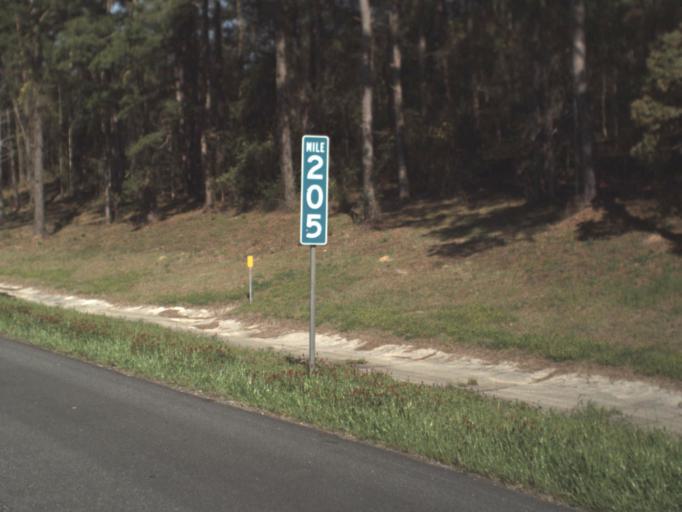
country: US
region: Florida
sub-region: Leon County
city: Tallahassee
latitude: 30.4984
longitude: -84.2070
